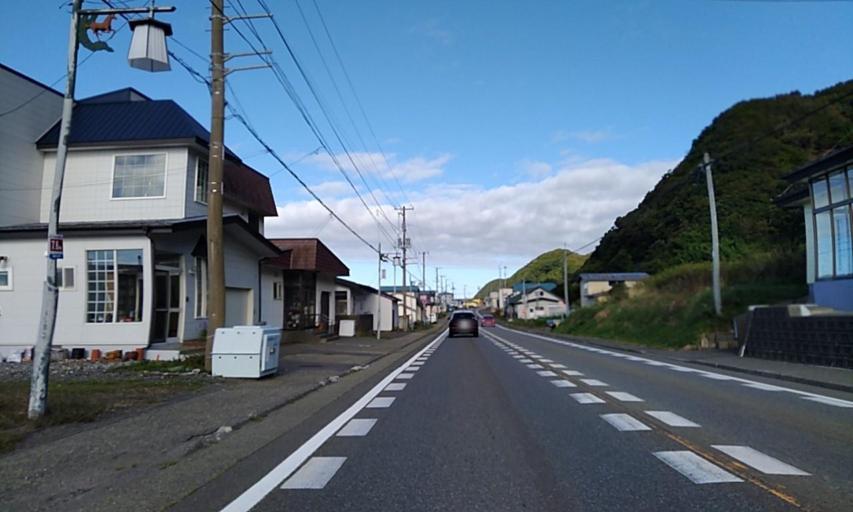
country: JP
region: Hokkaido
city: Shizunai-furukawacho
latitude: 42.2519
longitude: 142.5428
